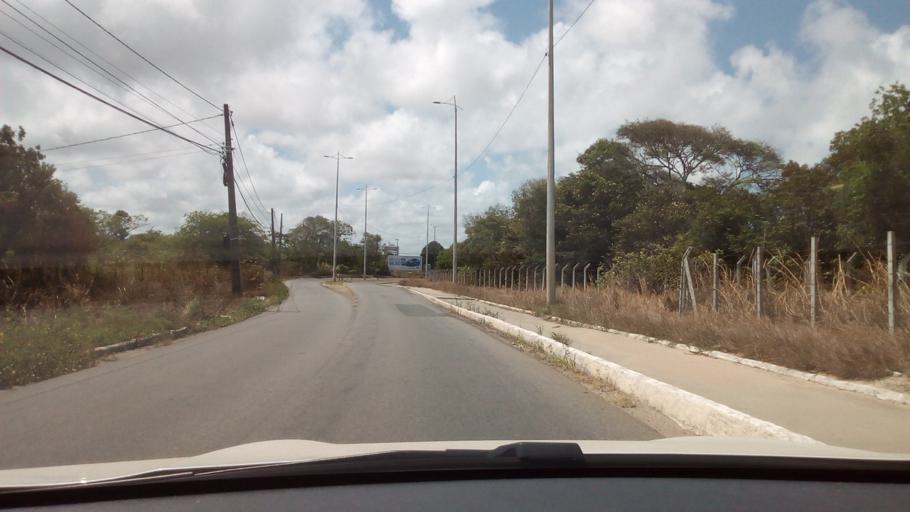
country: BR
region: Paraiba
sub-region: Joao Pessoa
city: Joao Pessoa
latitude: -7.1447
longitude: -34.8146
